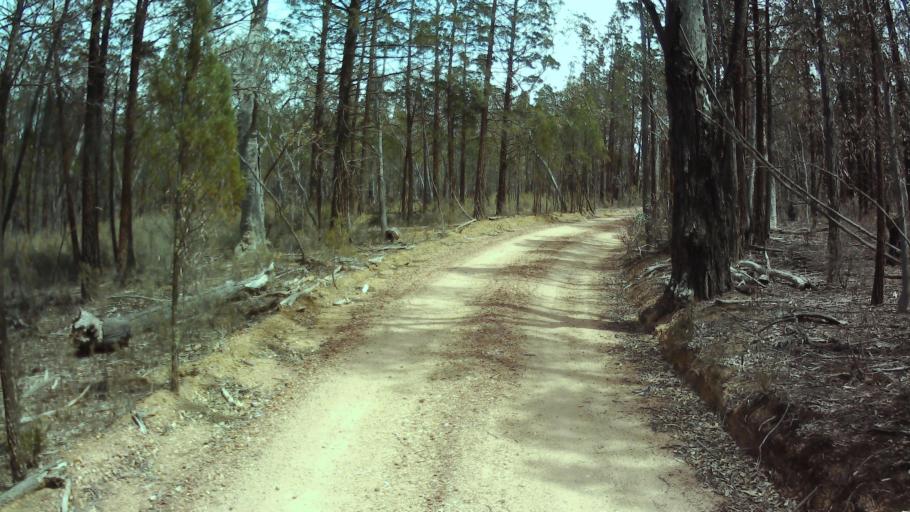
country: AU
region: New South Wales
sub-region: Weddin
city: Grenfell
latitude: -33.8905
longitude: 148.3870
